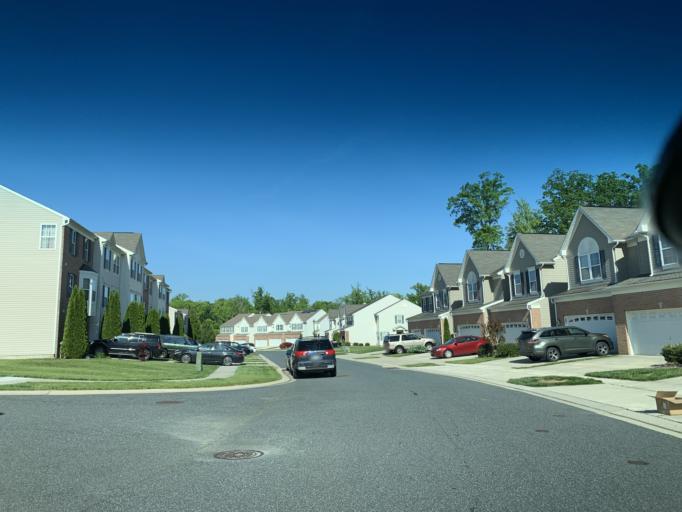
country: US
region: Maryland
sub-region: Harford County
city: Riverside
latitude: 39.4925
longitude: -76.2213
